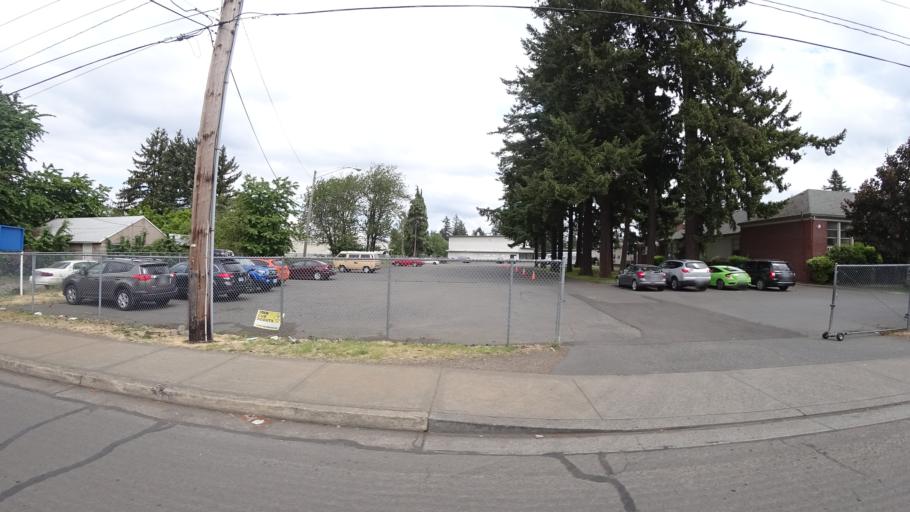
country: US
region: Oregon
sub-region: Multnomah County
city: Fairview
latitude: 45.5176
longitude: -122.4758
